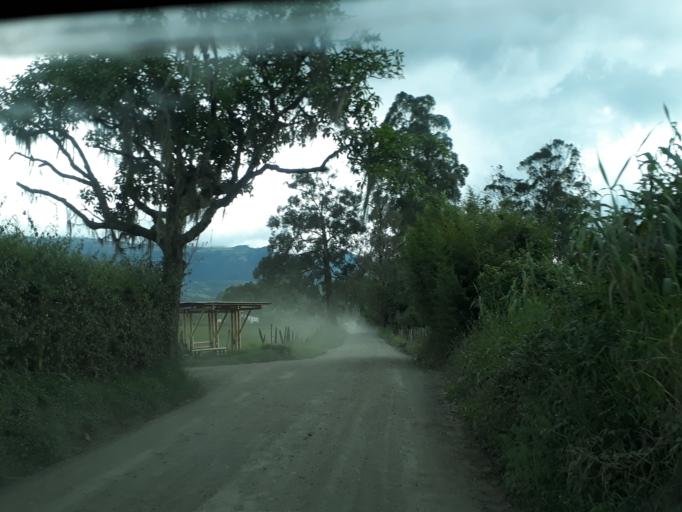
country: CO
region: Cundinamarca
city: Pacho
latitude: 5.1704
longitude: -74.1239
